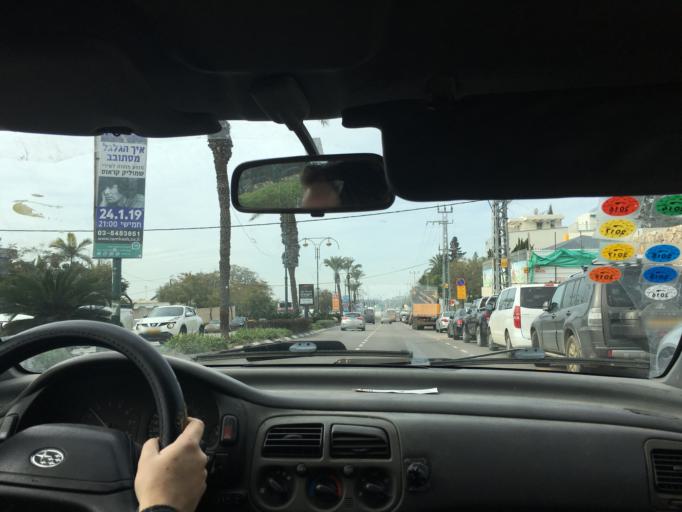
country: IL
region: Tel Aviv
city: Ramat HaSharon
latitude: 32.1376
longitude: 34.8381
